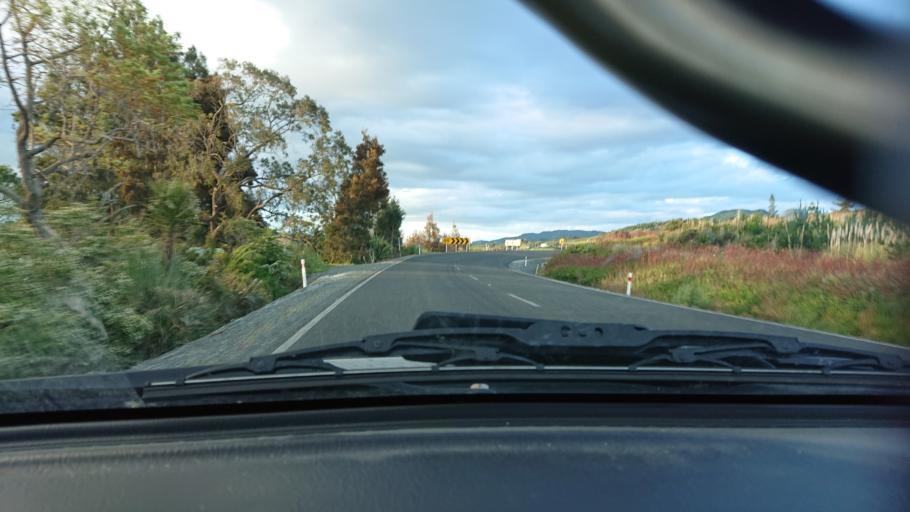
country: NZ
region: Auckland
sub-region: Auckland
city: Parakai
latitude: -36.5126
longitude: 174.4525
